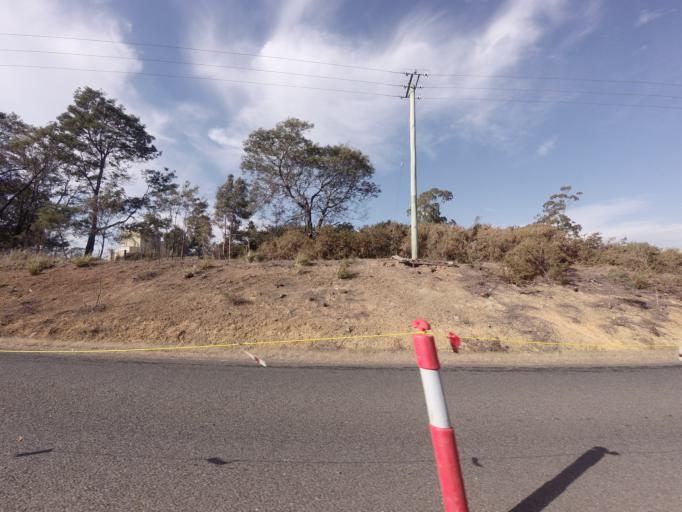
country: AU
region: Tasmania
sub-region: Northern Midlands
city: Longford
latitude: -41.5564
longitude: 146.9871
